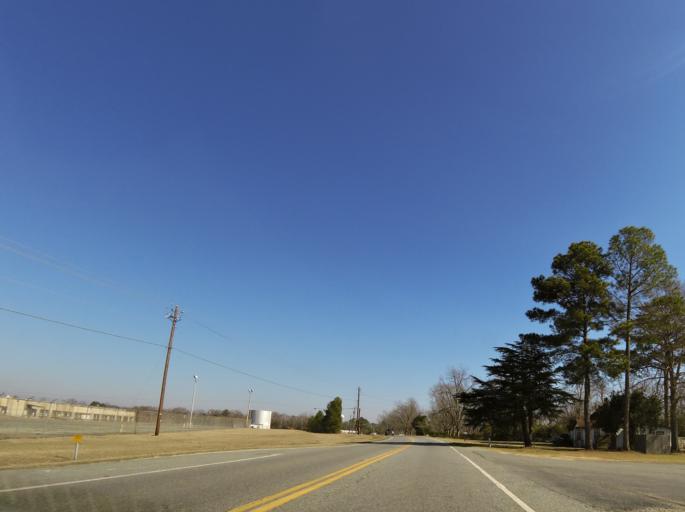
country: US
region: Georgia
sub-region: Bleckley County
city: Cochran
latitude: 32.3744
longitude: -83.3683
